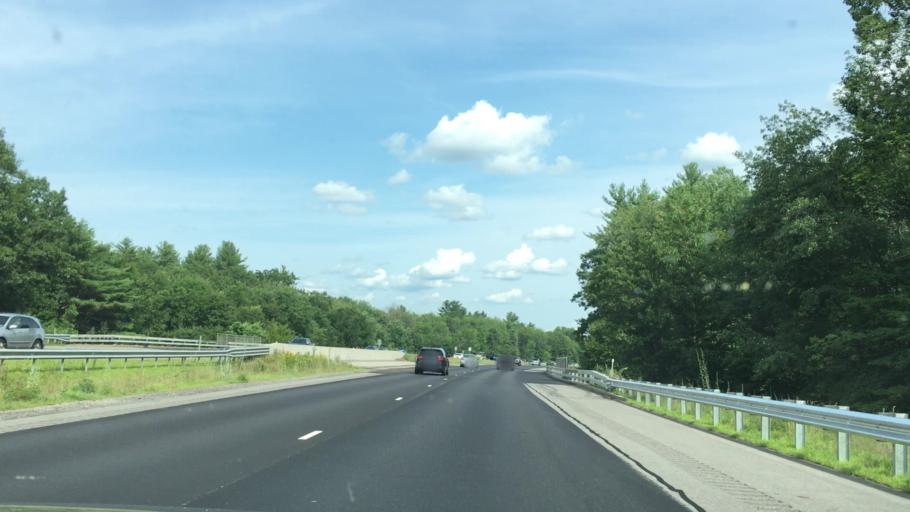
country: US
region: New Hampshire
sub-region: Merrimack County
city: Concord
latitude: 43.1829
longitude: -71.5752
